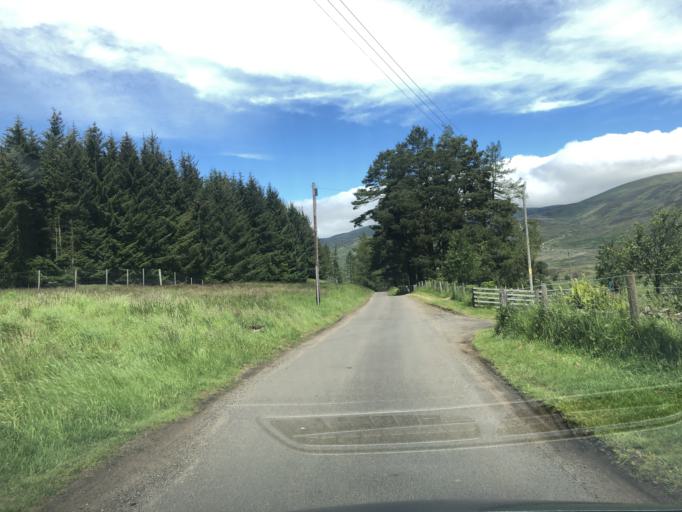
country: GB
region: Scotland
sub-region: Angus
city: Kirriemuir
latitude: 56.8163
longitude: -3.0575
